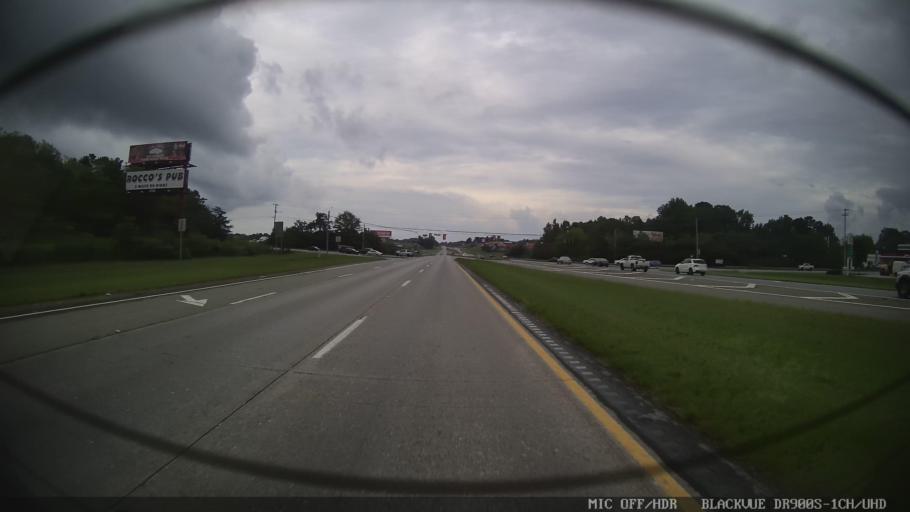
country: US
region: Georgia
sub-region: Pickens County
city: Jasper
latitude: 34.4664
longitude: -84.4582
